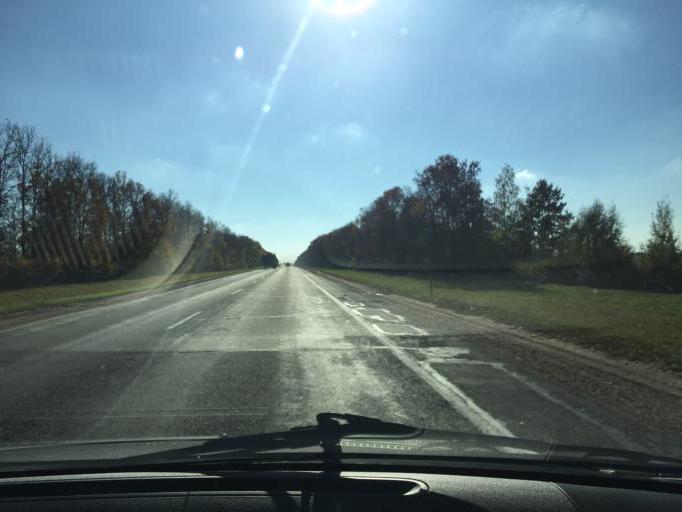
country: BY
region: Minsk
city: Slutsk
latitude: 52.9704
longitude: 27.5007
